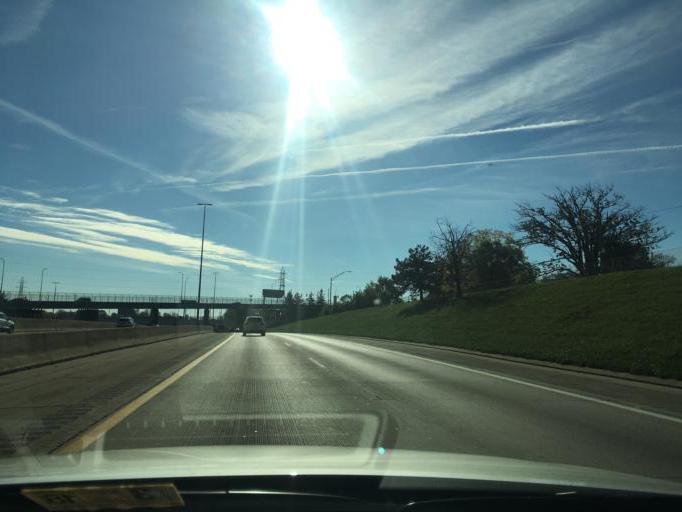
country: US
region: Michigan
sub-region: Wayne County
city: Dearborn Heights
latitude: 42.3819
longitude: -83.2390
